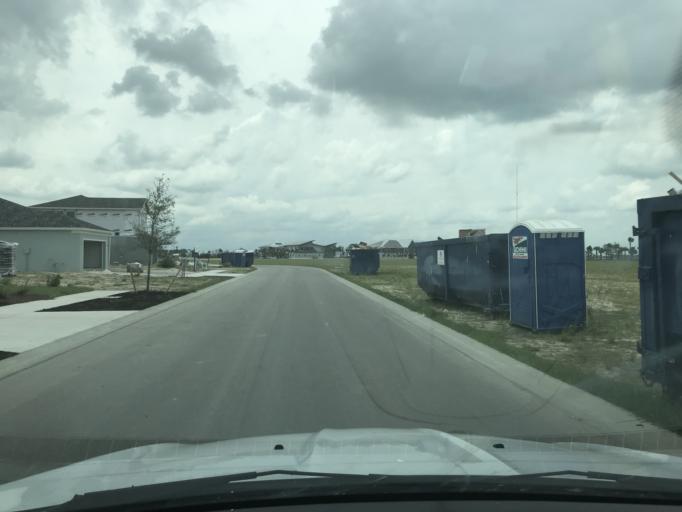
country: US
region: Florida
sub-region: Lee County
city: Olga
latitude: 26.7815
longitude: -81.7426
